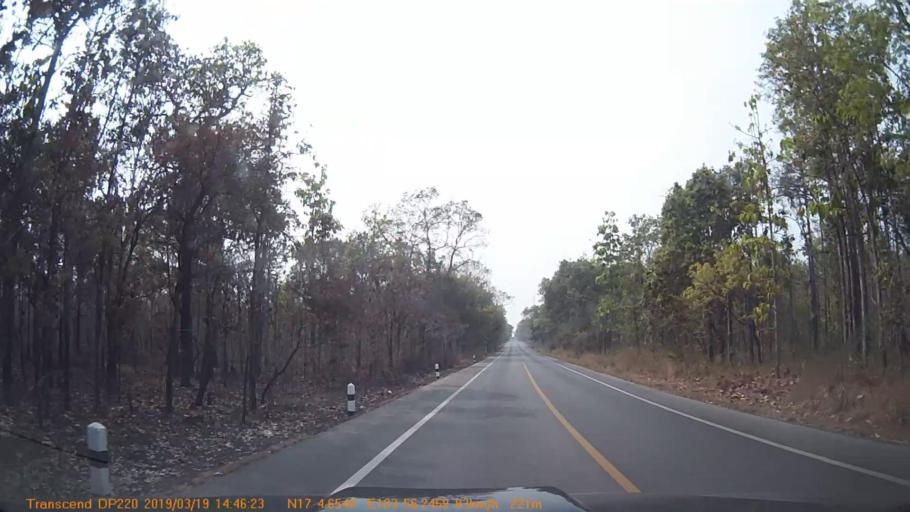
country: TH
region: Sakon Nakhon
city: Phu Phan
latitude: 17.0777
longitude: 103.9372
